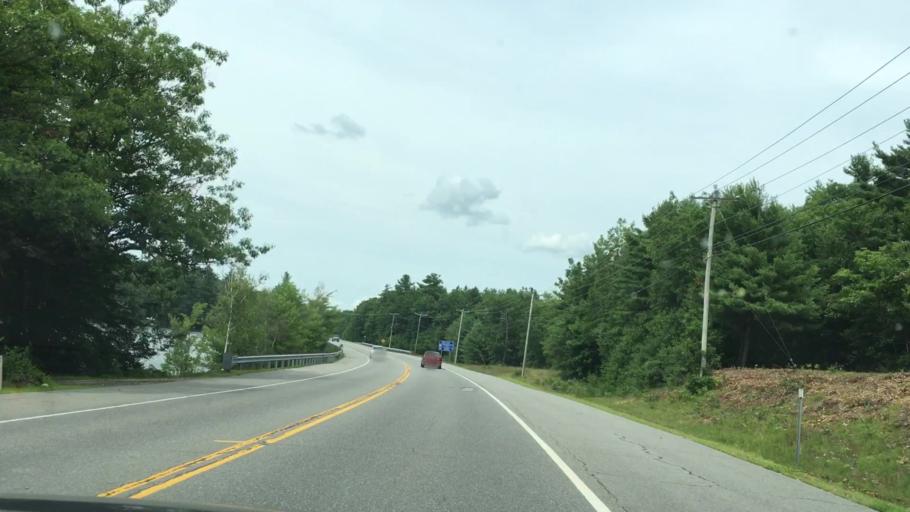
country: US
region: New Hampshire
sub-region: Cheshire County
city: Rindge
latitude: 42.7745
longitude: -72.0330
